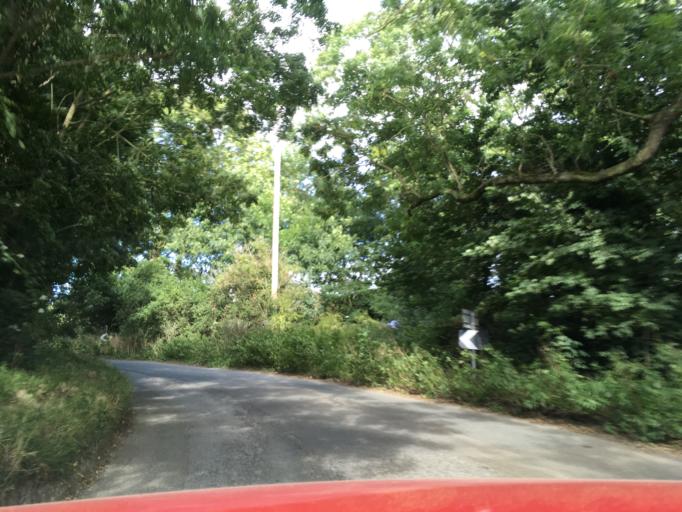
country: GB
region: England
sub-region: Gloucestershire
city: Stonehouse
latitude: 51.7789
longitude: -2.2788
